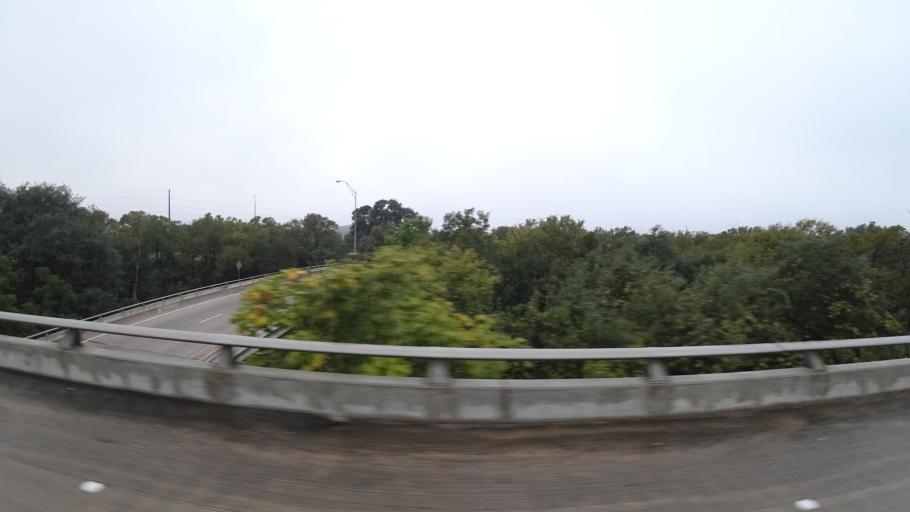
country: US
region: Texas
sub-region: Travis County
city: Rollingwood
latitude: 30.2759
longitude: -97.7681
